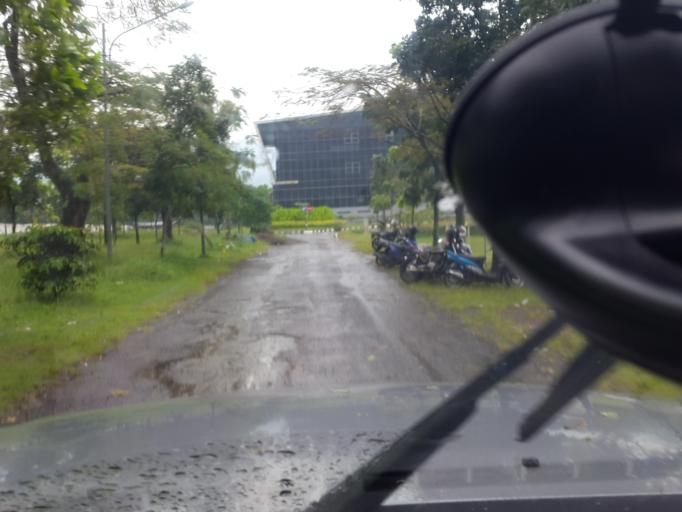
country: ID
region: West Java
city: Bandung
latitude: -6.9117
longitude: 107.6840
